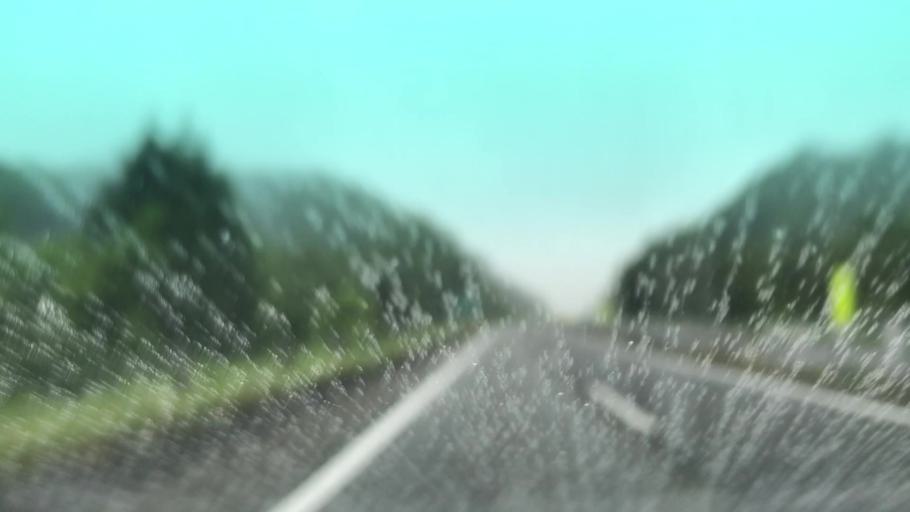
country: JP
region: Hokkaido
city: Shiraoi
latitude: 42.5574
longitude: 141.3159
